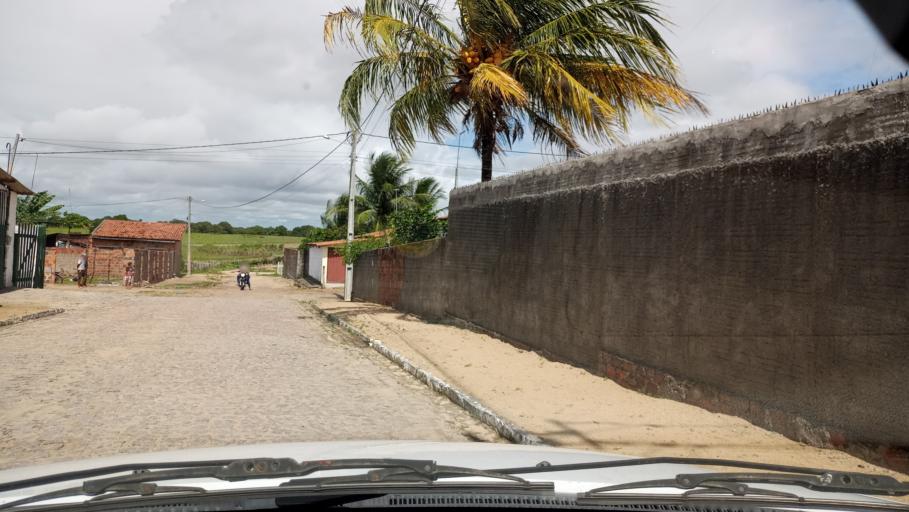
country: BR
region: Rio Grande do Norte
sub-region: Brejinho
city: Brejinho
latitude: -6.1575
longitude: -35.4387
